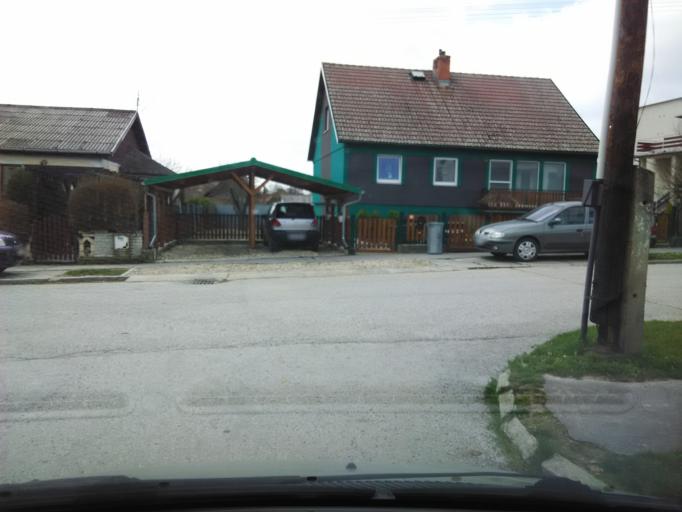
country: SK
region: Nitriansky
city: Zlate Moravce
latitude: 48.4170
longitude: 18.3604
